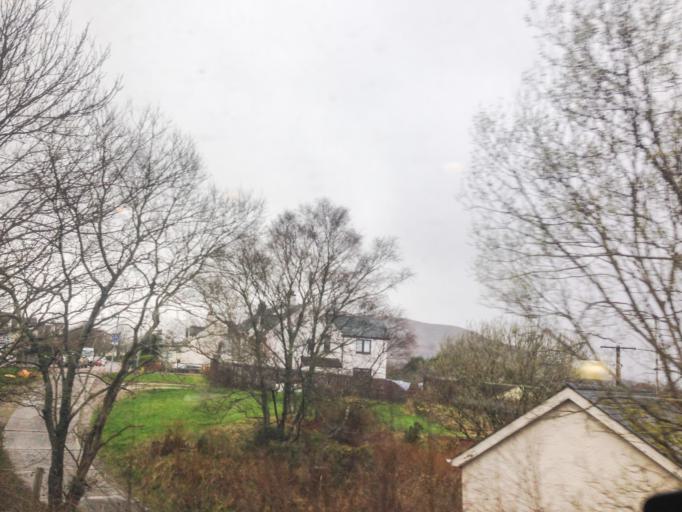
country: GB
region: Scotland
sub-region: Highland
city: Fort William
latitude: 56.8280
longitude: -5.0880
